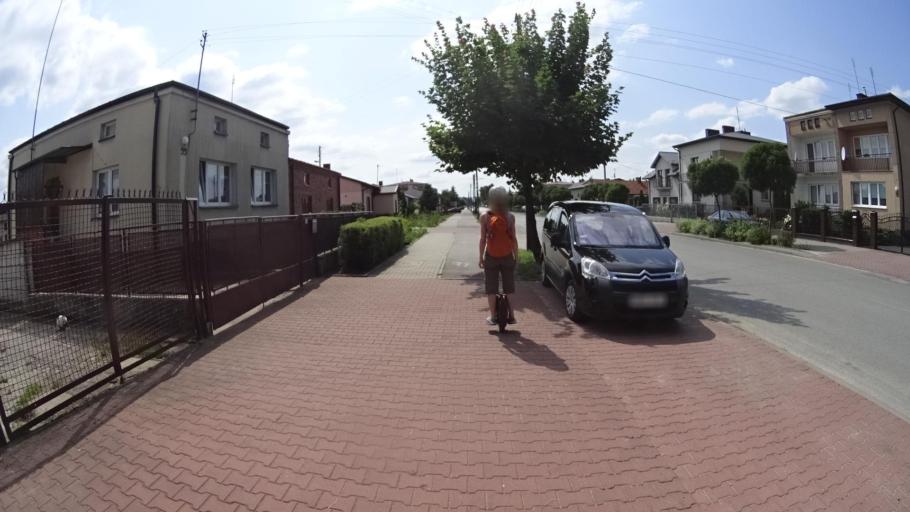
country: PL
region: Masovian Voivodeship
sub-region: Powiat bialobrzeski
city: Bialobrzegi
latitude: 51.6486
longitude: 20.9469
